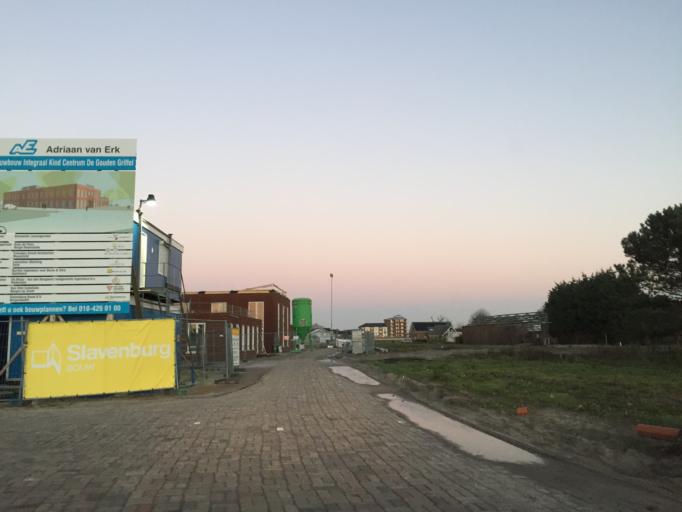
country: NL
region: South Holland
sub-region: Gemeente Lansingerland
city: Berkel en Rodenrijs
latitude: 51.9843
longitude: 4.4509
